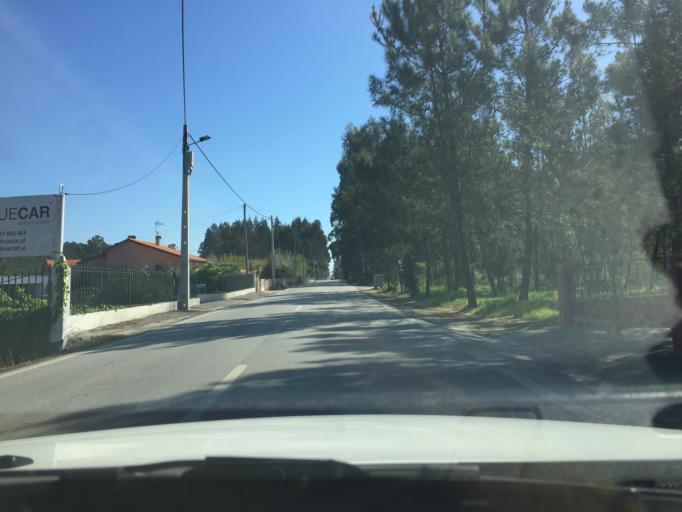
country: PT
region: Coimbra
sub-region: Cantanhede
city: Cantanhede
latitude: 40.4194
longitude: -8.5509
